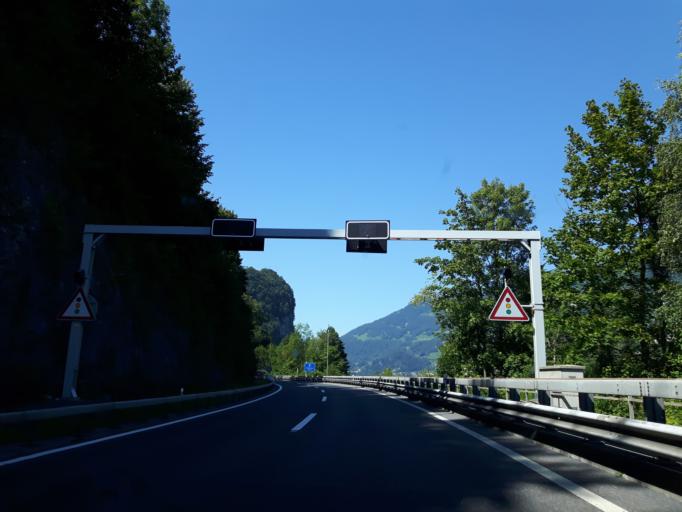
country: CH
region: Saint Gallen
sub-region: Wahlkreis See-Gaster
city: Amden
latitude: 47.1220
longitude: 9.1561
